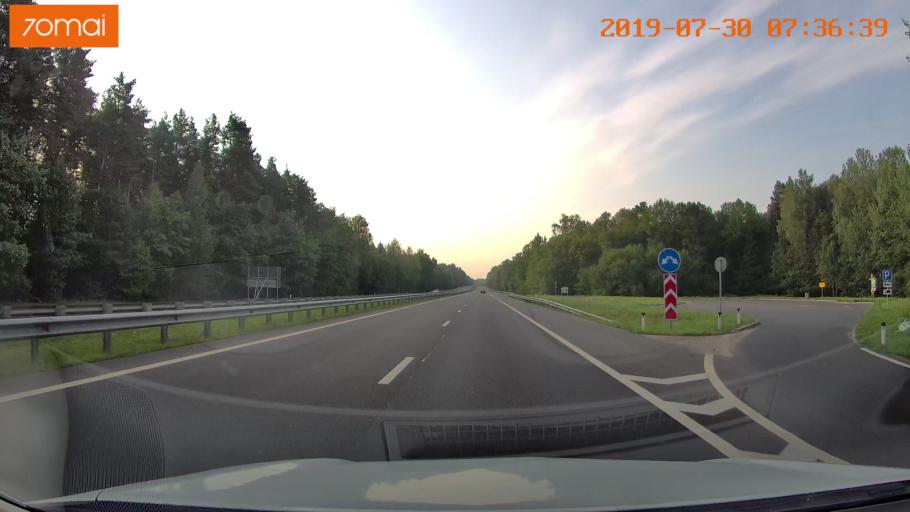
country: RU
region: Kaliningrad
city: Gvardeysk
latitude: 54.6626
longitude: 21.1292
